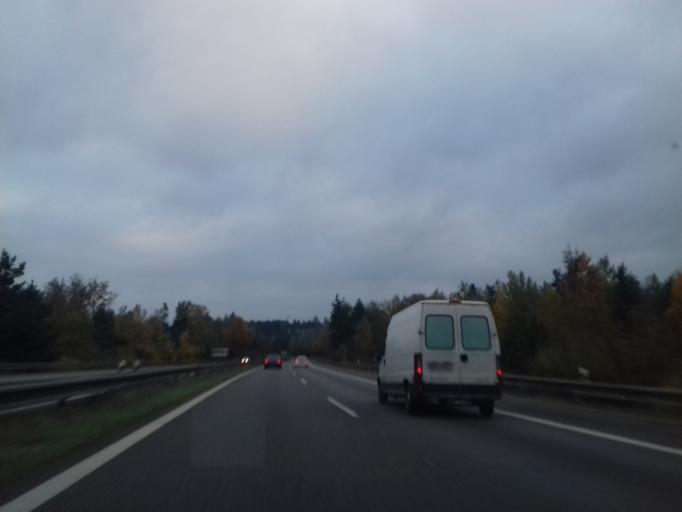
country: CZ
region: Central Bohemia
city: Zruc nad Sazavou
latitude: 49.6996
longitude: 15.0906
